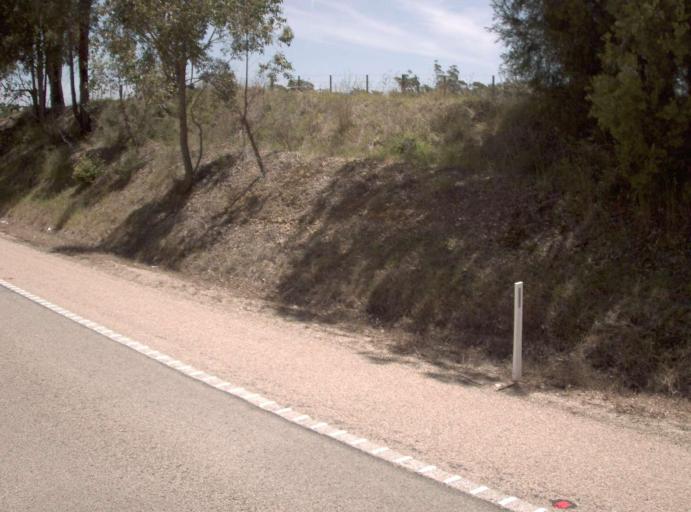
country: AU
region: Victoria
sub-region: East Gippsland
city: Bairnsdale
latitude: -37.7511
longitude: 147.7471
